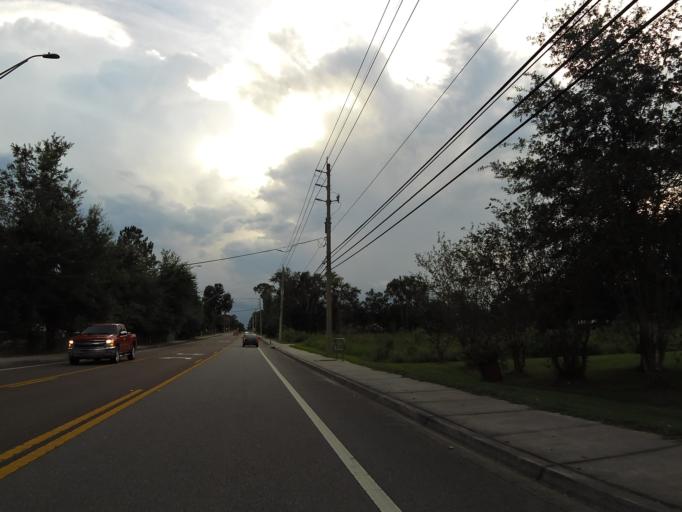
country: US
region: Florida
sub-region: Clay County
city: Bellair-Meadowbrook Terrace
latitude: 30.3023
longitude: -81.8137
